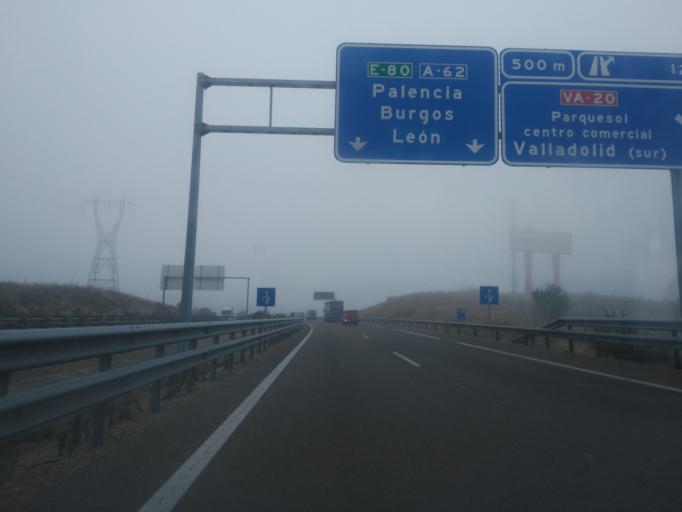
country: ES
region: Castille and Leon
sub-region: Provincia de Valladolid
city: Arroyo
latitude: 41.6287
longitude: -4.7812
